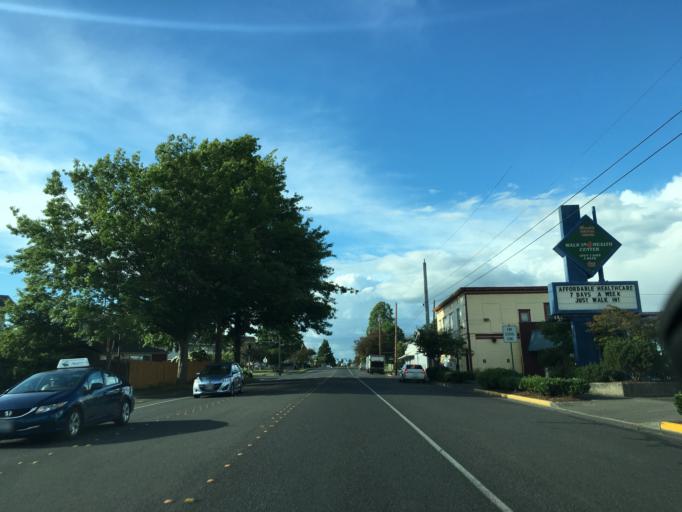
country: US
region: Washington
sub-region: Whatcom County
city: Bellingham
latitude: 48.7597
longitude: -122.4751
